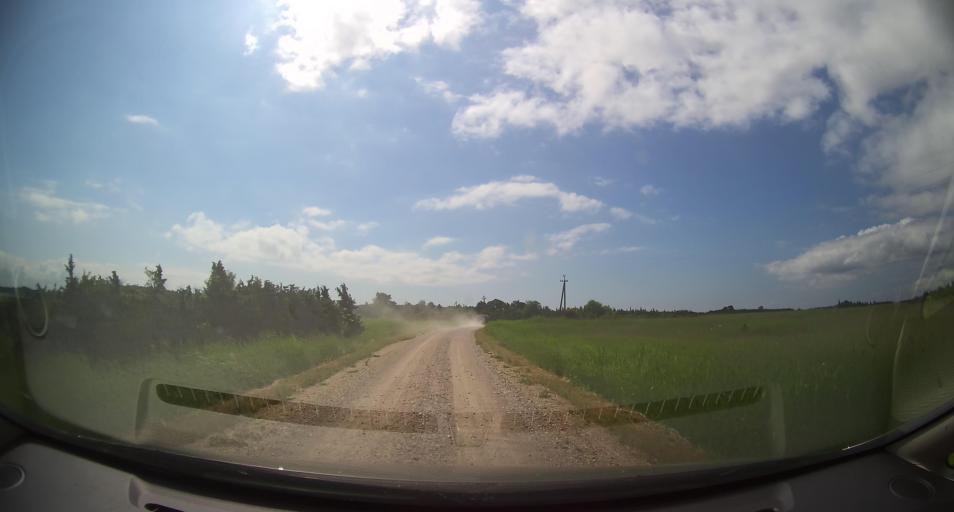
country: EE
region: Laeaene
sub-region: Lihula vald
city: Lihula
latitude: 58.5684
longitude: 23.5465
